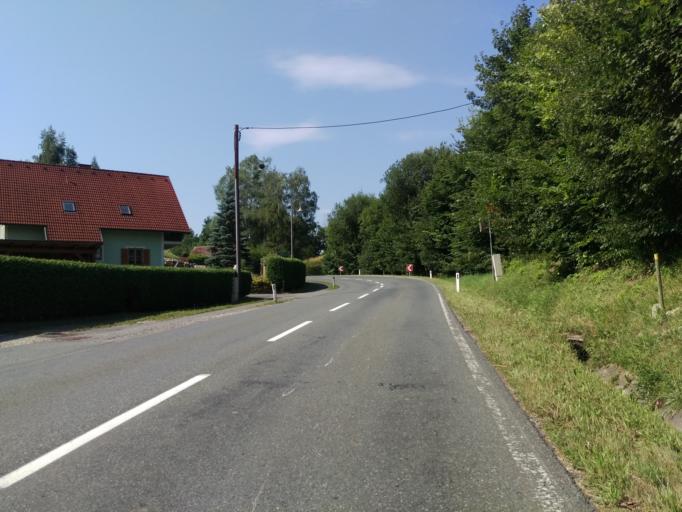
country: AT
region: Styria
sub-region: Politischer Bezirk Graz-Umgebung
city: Mellach
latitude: 46.9405
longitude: 15.5107
